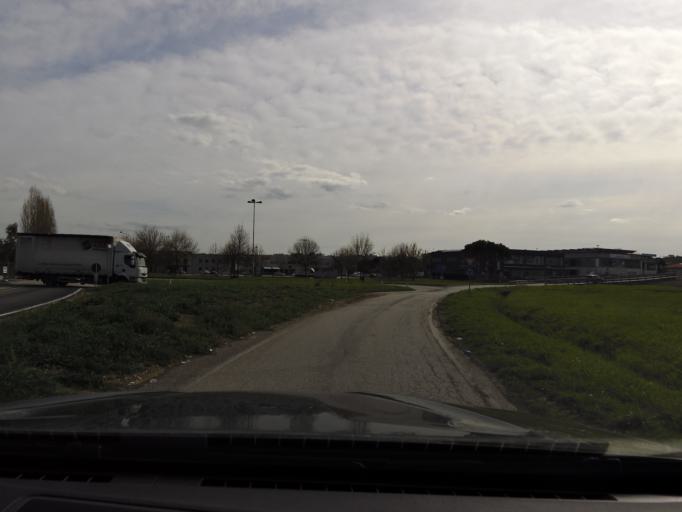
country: IT
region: The Marches
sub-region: Provincia di Ancona
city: Camerano
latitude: 43.5167
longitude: 13.5303
